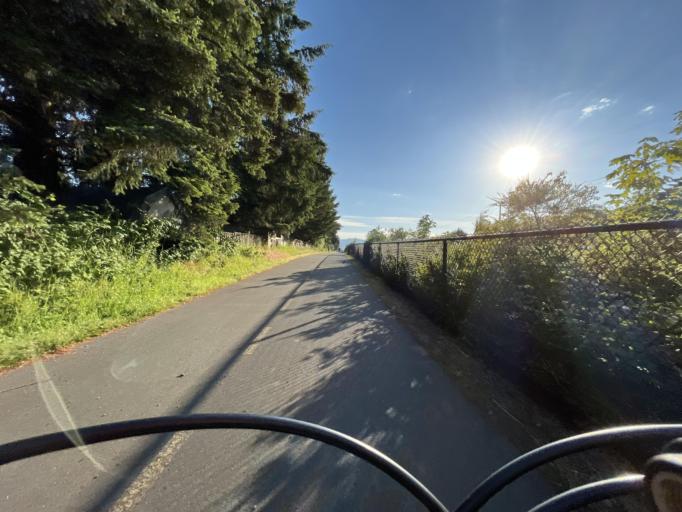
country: CA
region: British Columbia
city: Langford
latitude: 48.4488
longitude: -123.4876
